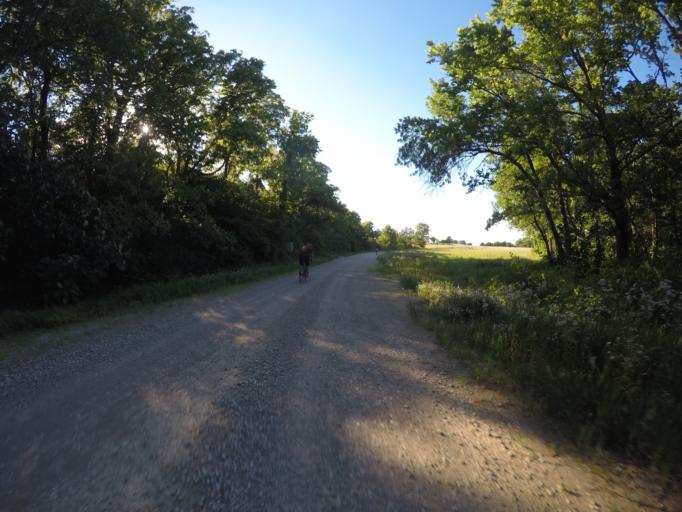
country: US
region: Kansas
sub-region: Riley County
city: Ogden
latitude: 39.2494
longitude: -96.7372
